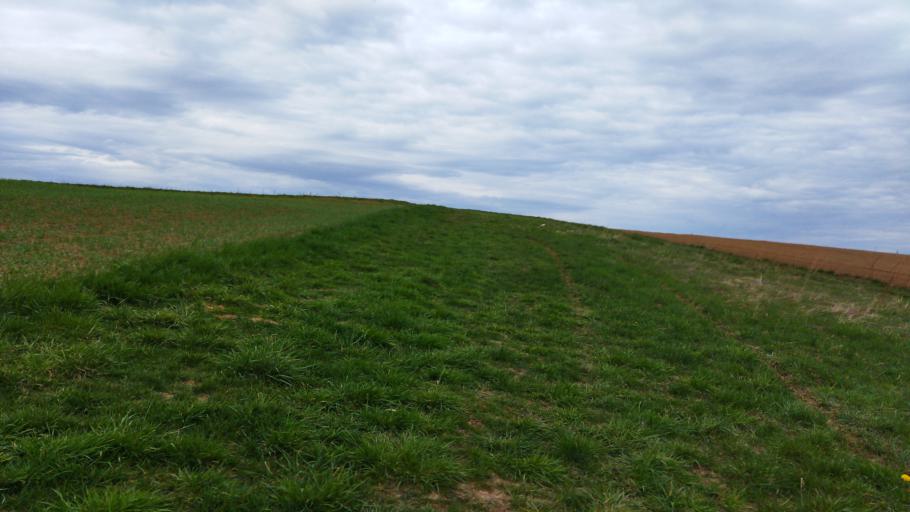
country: DE
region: Baden-Wuerttemberg
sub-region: Regierungsbezirk Stuttgart
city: Oedheim
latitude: 49.2205
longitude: 9.2828
